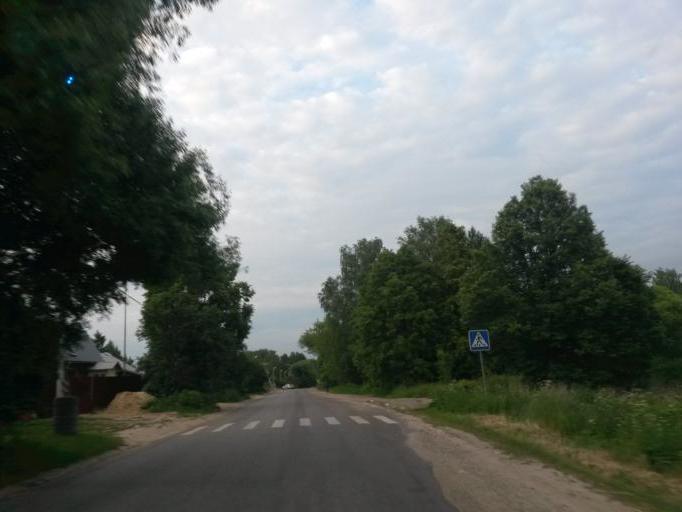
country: RU
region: Moskovskaya
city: Lyubuchany
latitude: 55.2563
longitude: 37.6009
